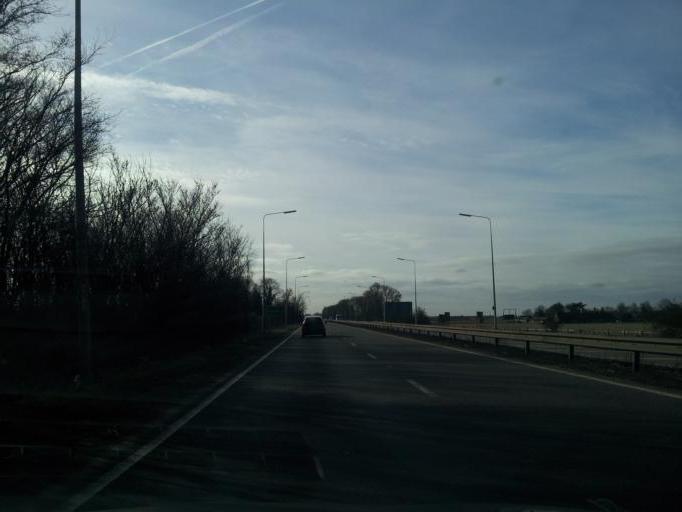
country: GB
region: England
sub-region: Central Bedfordshire
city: Biggleswade
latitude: 52.0901
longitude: -0.2741
